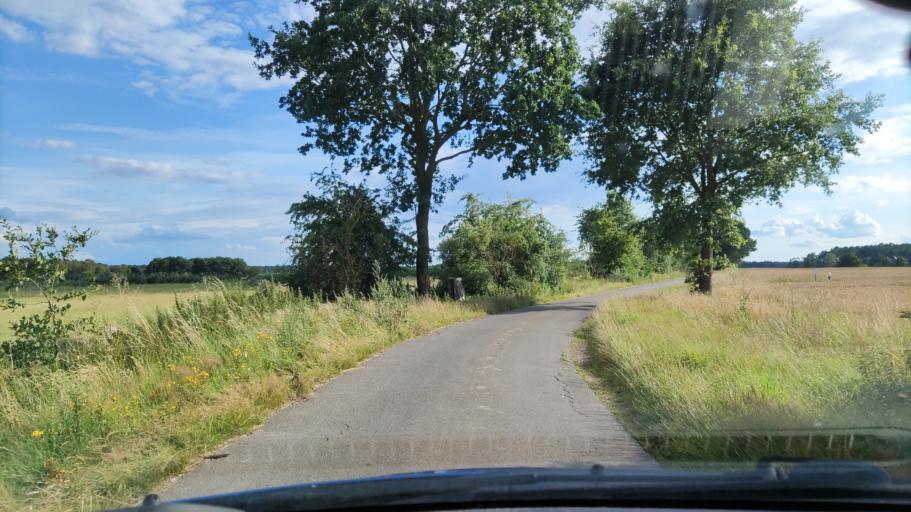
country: DE
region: Lower Saxony
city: Boitze
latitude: 53.1458
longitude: 10.7436
